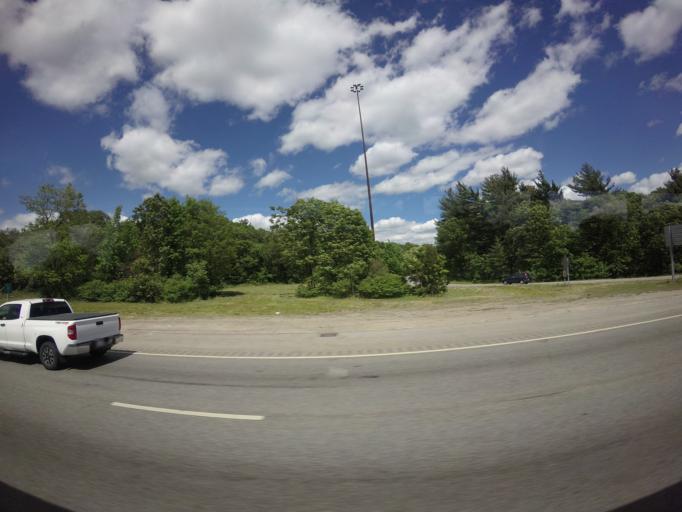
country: US
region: Massachusetts
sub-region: Middlesex County
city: Stoneham
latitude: 42.5036
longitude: -71.1193
